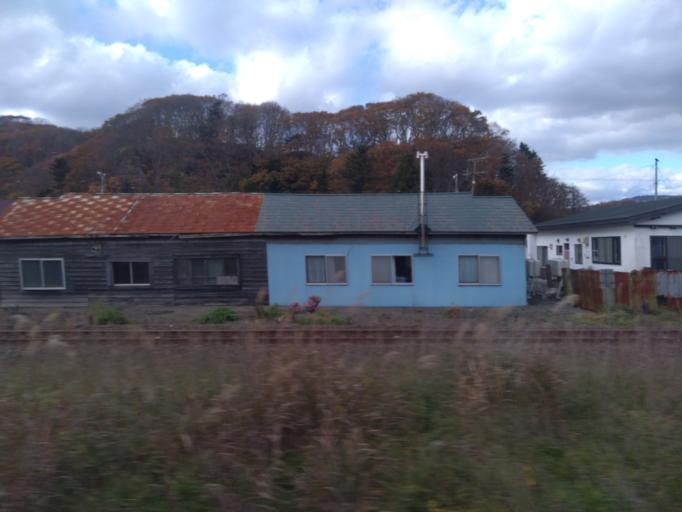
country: JP
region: Hokkaido
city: Niseko Town
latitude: 42.5848
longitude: 140.6355
